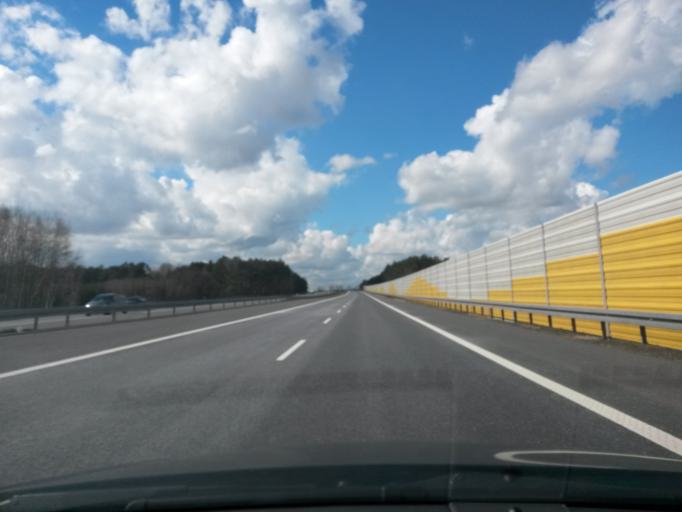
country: PL
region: Lodz Voivodeship
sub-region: Powiat leczycki
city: Swinice Warckie
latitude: 52.0233
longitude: 18.9251
